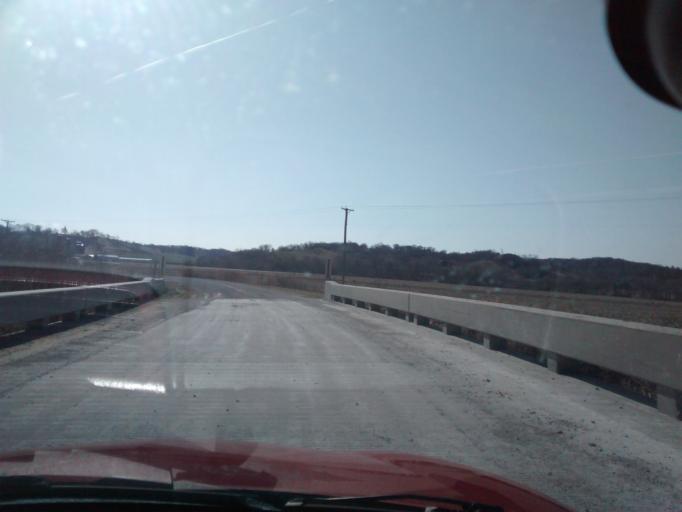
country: US
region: Iowa
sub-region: Pottawattamie County
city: Carter Lake
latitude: 41.3914
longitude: -95.8500
